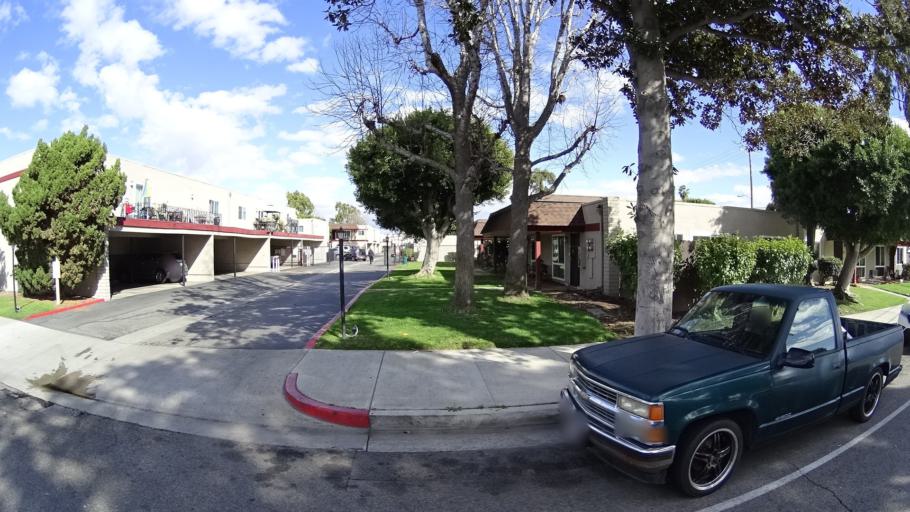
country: US
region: California
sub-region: Orange County
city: Anaheim
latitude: 33.8364
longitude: -117.9547
